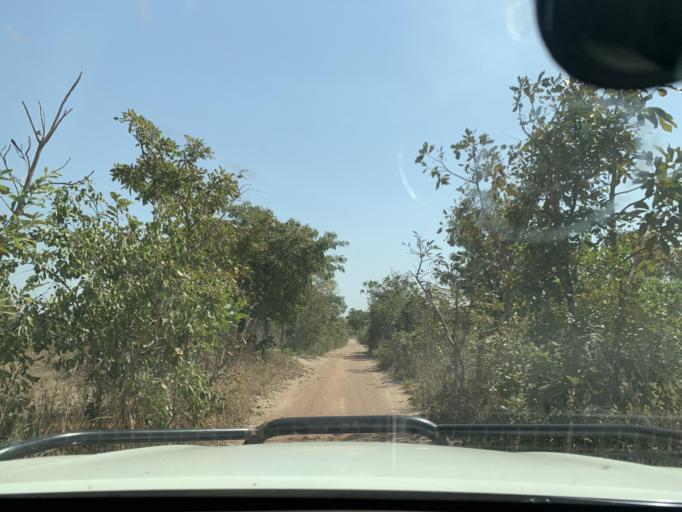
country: ML
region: Sikasso
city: Kolondieba
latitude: 10.8377
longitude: -6.7964
